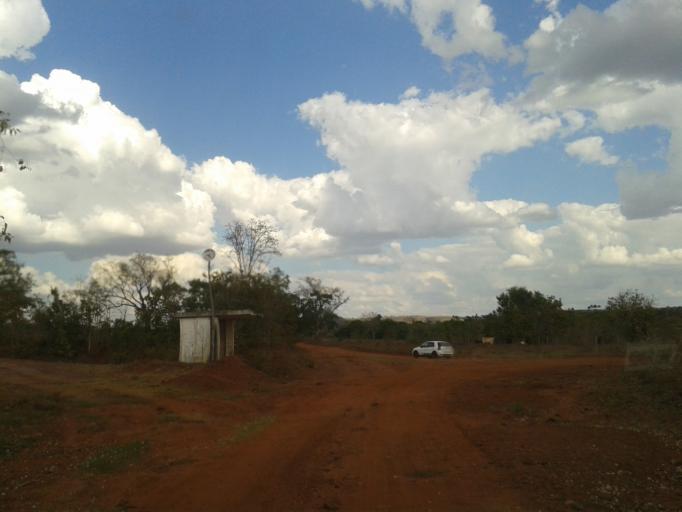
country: BR
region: Minas Gerais
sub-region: Santa Vitoria
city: Santa Vitoria
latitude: -19.2449
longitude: -49.9766
